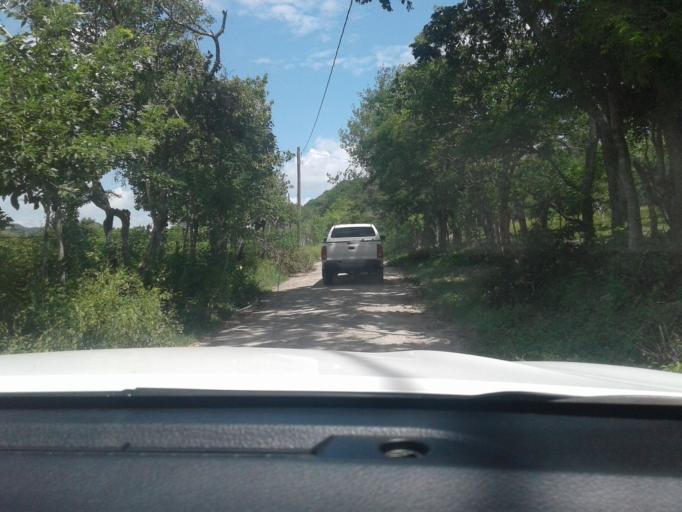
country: NI
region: Matagalpa
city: Terrabona
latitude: 12.5628
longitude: -86.0374
